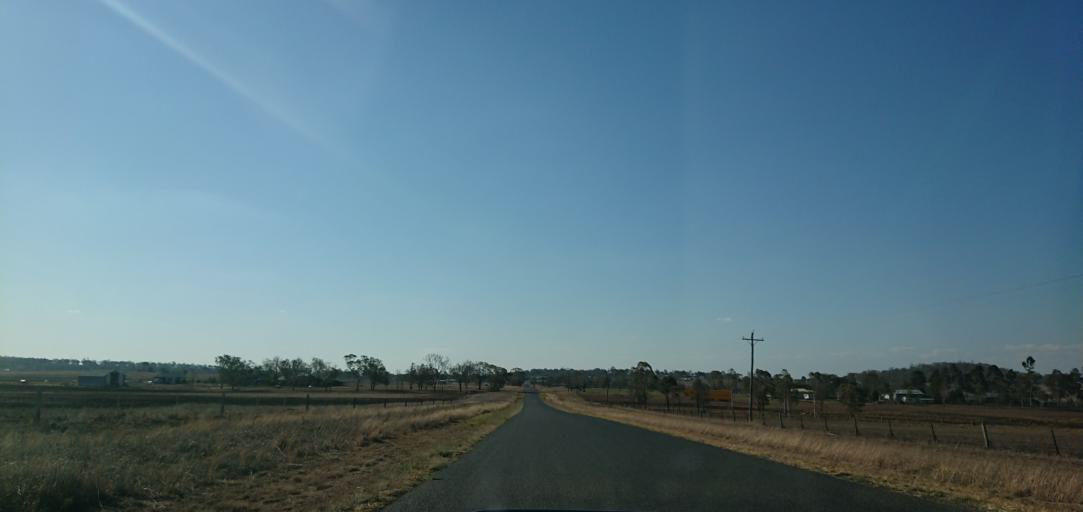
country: AU
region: Queensland
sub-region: Toowoomba
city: Westbrook
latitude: -27.6947
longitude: 151.7162
